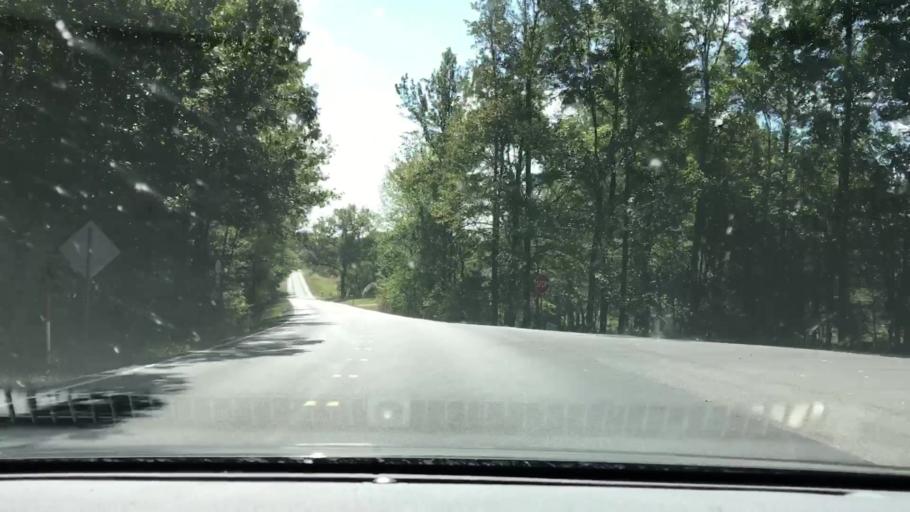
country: US
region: Kentucky
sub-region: Graves County
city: Mayfield
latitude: 36.8676
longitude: -88.5738
